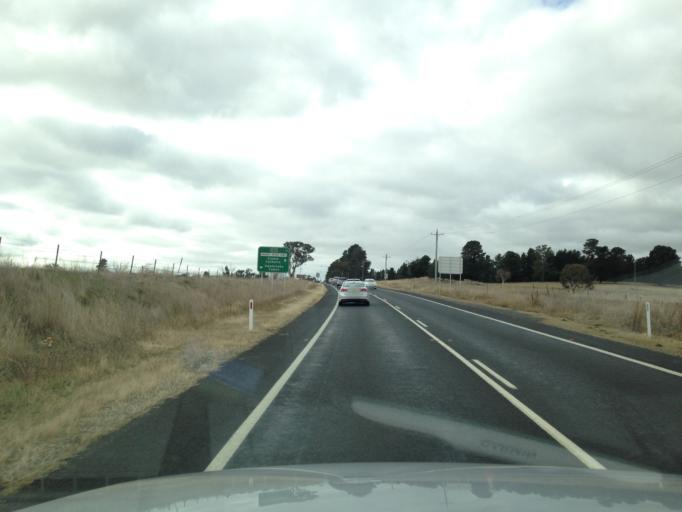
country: AU
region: New South Wales
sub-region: Cooma-Monaro
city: Cooma
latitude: -36.2486
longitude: 149.0474
